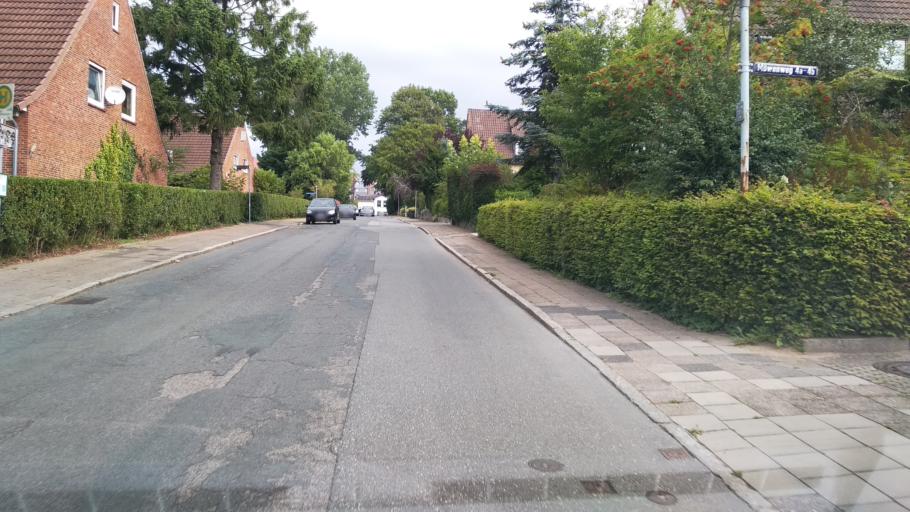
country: DE
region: Schleswig-Holstein
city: Schleswig
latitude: 54.5190
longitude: 9.5754
